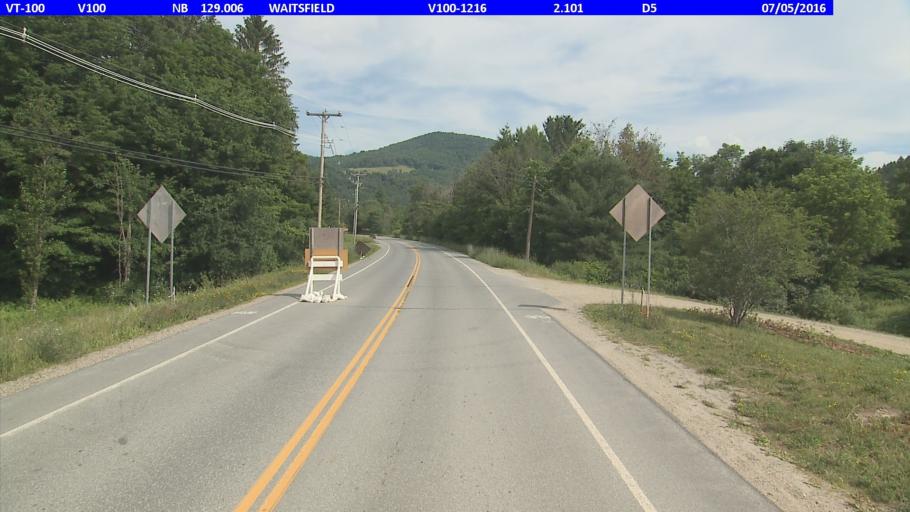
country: US
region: Vermont
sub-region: Washington County
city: Northfield
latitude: 44.1755
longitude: -72.8336
